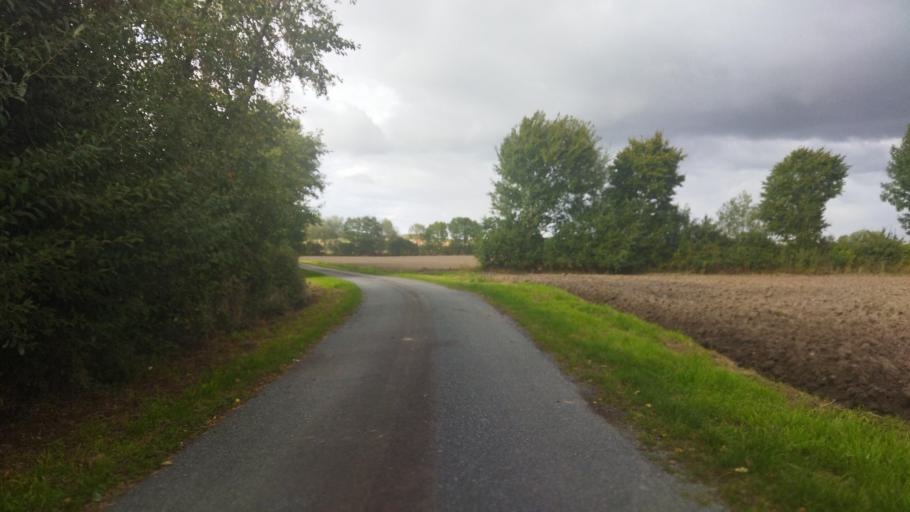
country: DE
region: North Rhine-Westphalia
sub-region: Regierungsbezirk Munster
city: Dulmen
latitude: 51.8994
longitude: 7.2613
